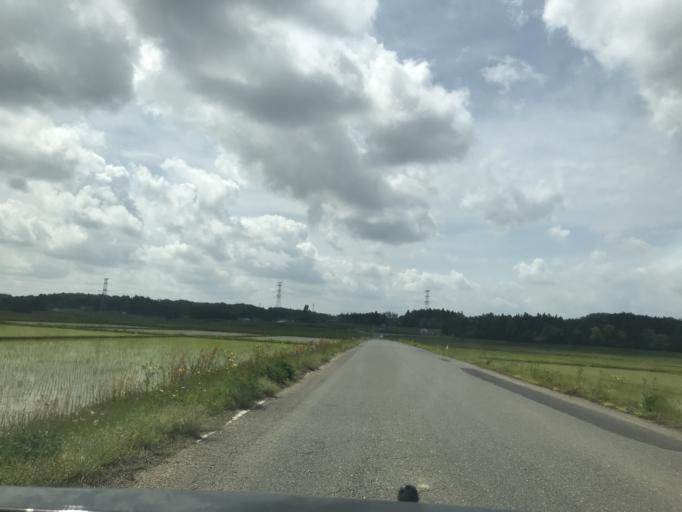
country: JP
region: Iwate
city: Ichinoseki
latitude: 38.8222
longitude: 141.0203
